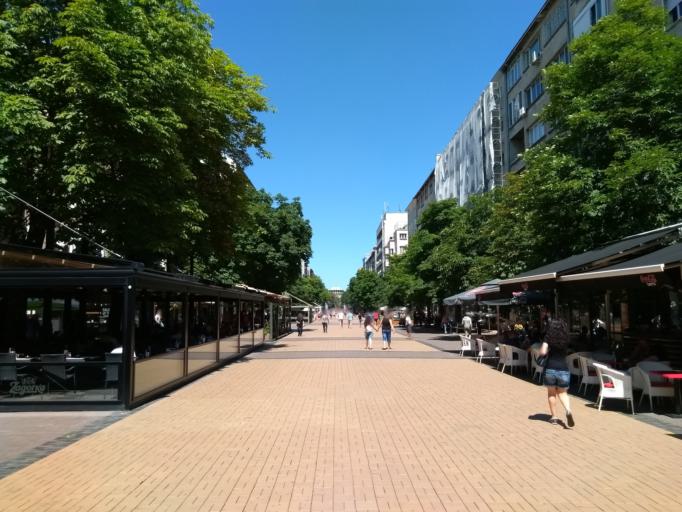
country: BG
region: Sofia-Capital
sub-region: Stolichna Obshtina
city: Sofia
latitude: 42.6918
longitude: 23.3198
